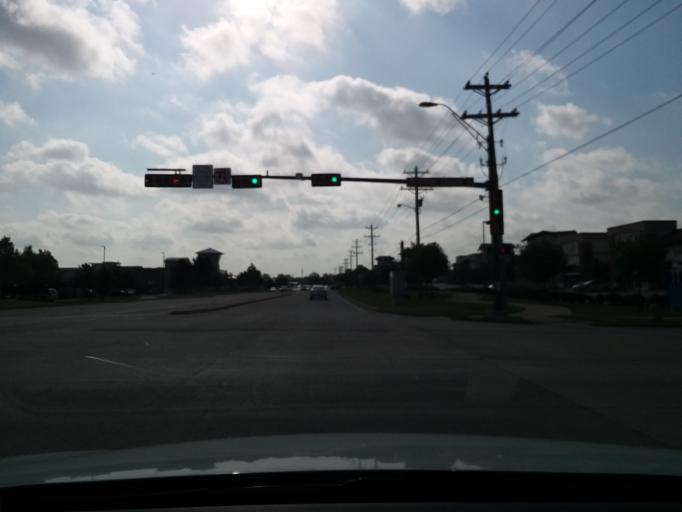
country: US
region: Texas
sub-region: Denton County
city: Double Oak
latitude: 33.0719
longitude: -97.0881
